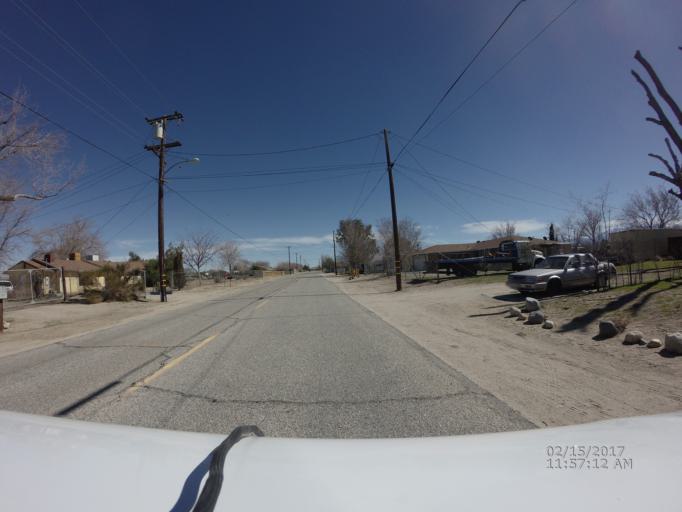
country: US
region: California
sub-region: Los Angeles County
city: Littlerock
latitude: 34.5743
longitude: -117.9501
